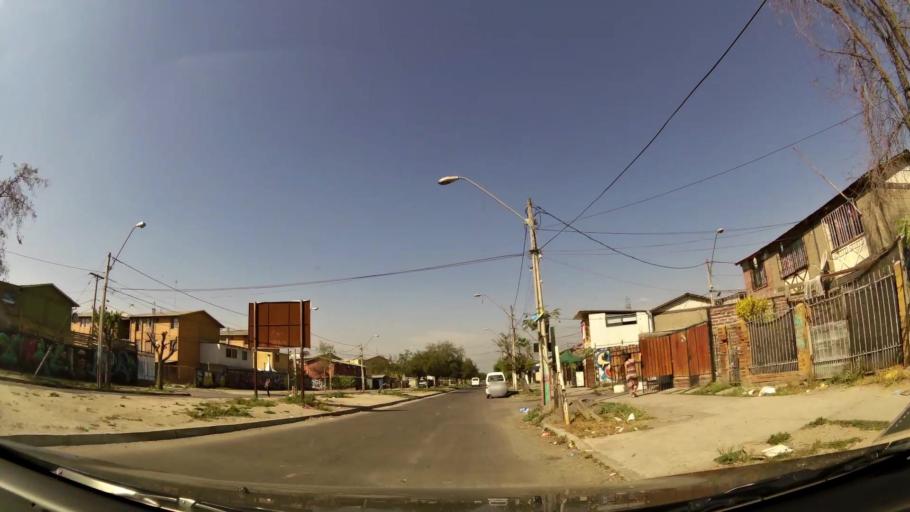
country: CL
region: Santiago Metropolitan
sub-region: Provincia de Santiago
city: La Pintana
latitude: -33.6235
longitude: -70.6231
